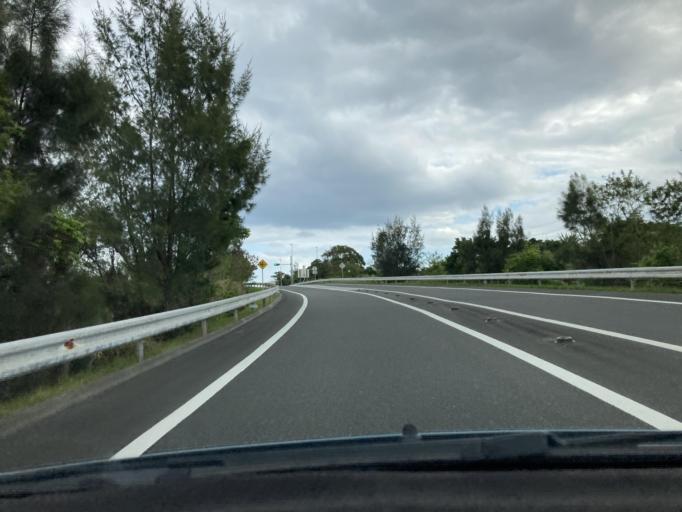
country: JP
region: Okinawa
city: Nago
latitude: 26.4847
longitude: 127.9691
